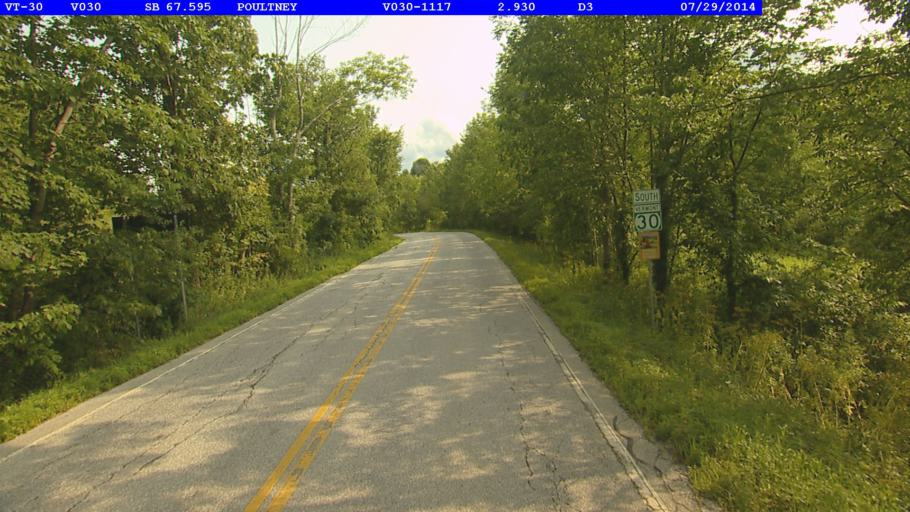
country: US
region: Vermont
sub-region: Rutland County
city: Poultney
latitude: 43.5037
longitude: -73.2099
